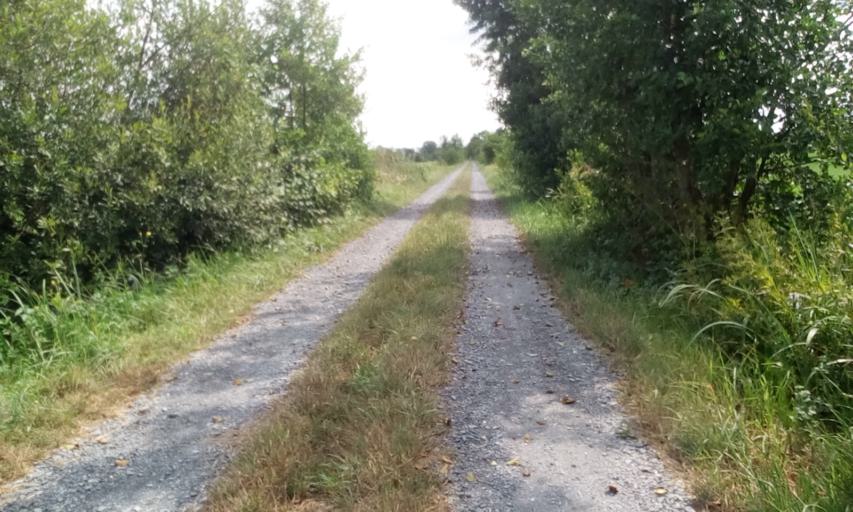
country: FR
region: Lower Normandy
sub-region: Departement du Calvados
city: Bavent
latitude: 49.2268
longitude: -0.1720
